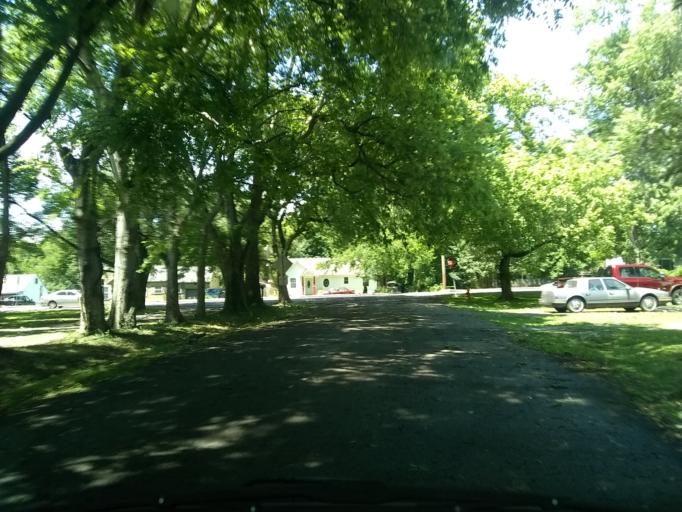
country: US
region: Tennessee
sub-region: Davidson County
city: Oak Hill
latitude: 36.1268
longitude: -86.7039
